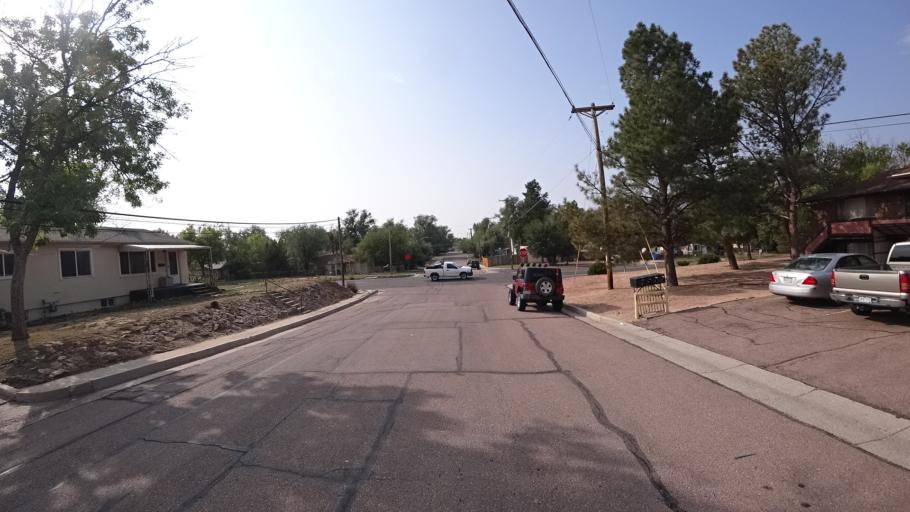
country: US
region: Colorado
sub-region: El Paso County
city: Colorado Springs
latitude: 38.8414
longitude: -104.7827
